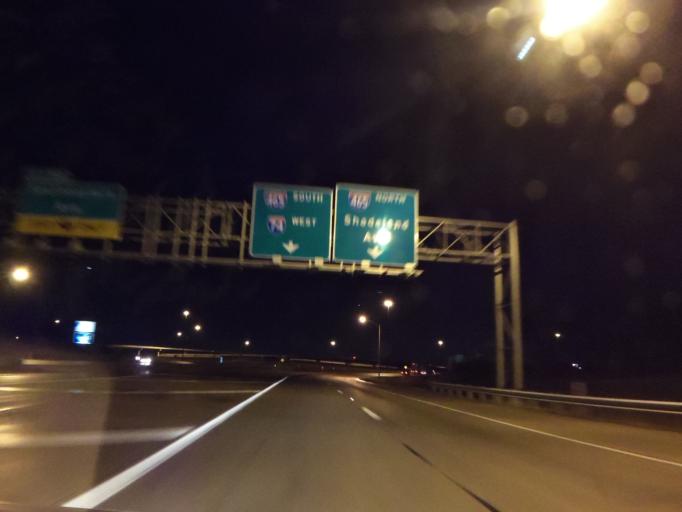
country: US
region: Indiana
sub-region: Marion County
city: Warren Park
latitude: 39.7324
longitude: -86.0377
